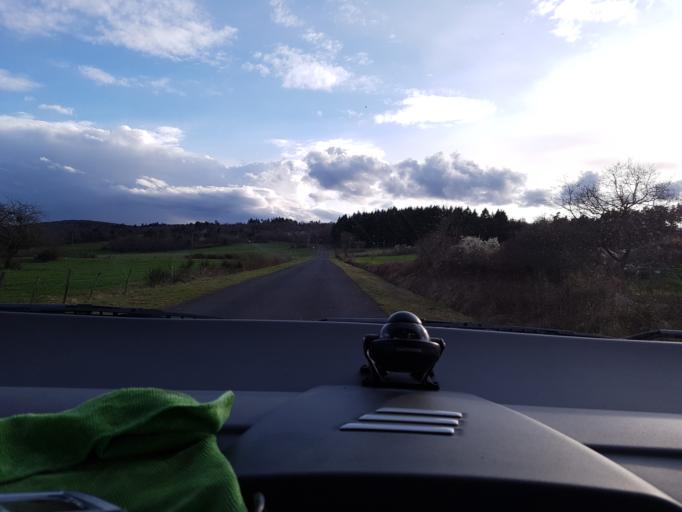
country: FR
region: Auvergne
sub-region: Departement de la Haute-Loire
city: Lempdes-sur-Allagnon
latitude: 45.3416
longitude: 3.2337
